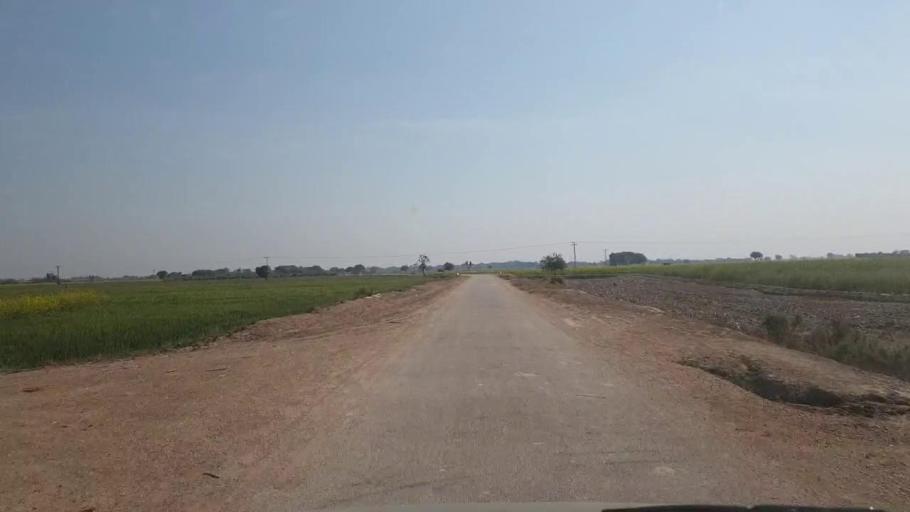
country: PK
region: Sindh
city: Chambar
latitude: 25.3728
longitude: 68.8140
